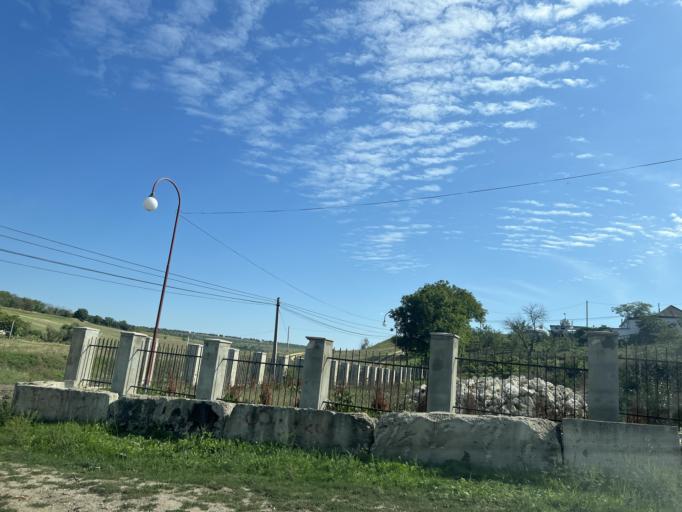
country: MD
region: Ungheni
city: Ungheni
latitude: 47.1953
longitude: 27.8132
